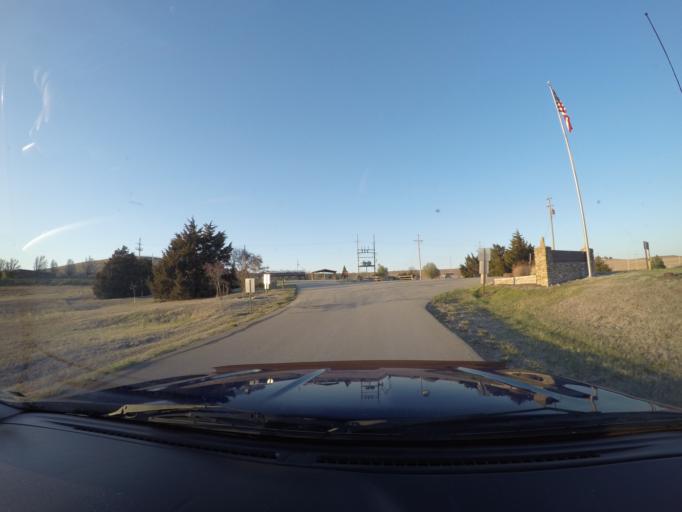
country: US
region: Kansas
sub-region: Wabaunsee County
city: Alma
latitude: 38.8690
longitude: -96.1900
